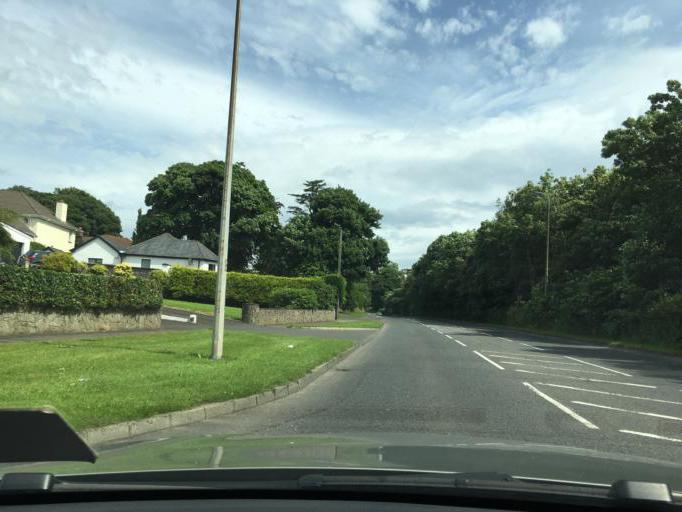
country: GB
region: Northern Ireland
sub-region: City of Derry
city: Derry
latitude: 55.0260
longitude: -7.3007
